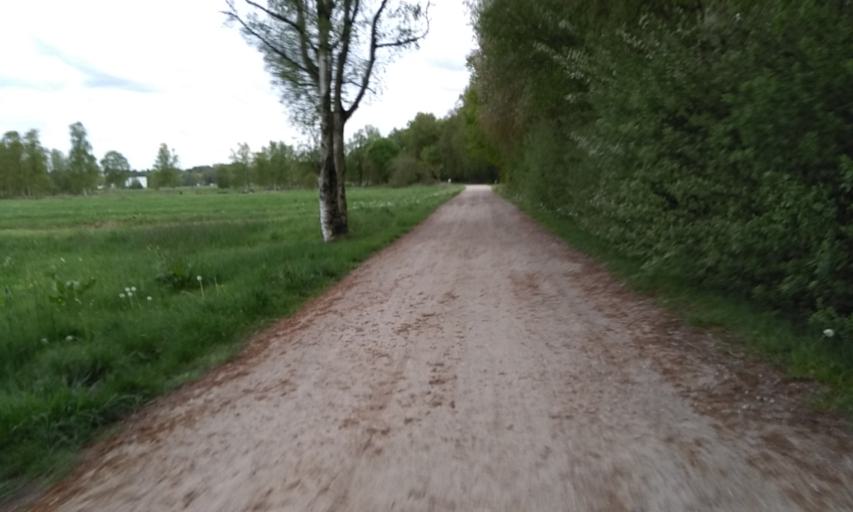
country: DE
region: Lower Saxony
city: Buxtehude
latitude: 53.4816
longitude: 9.6769
